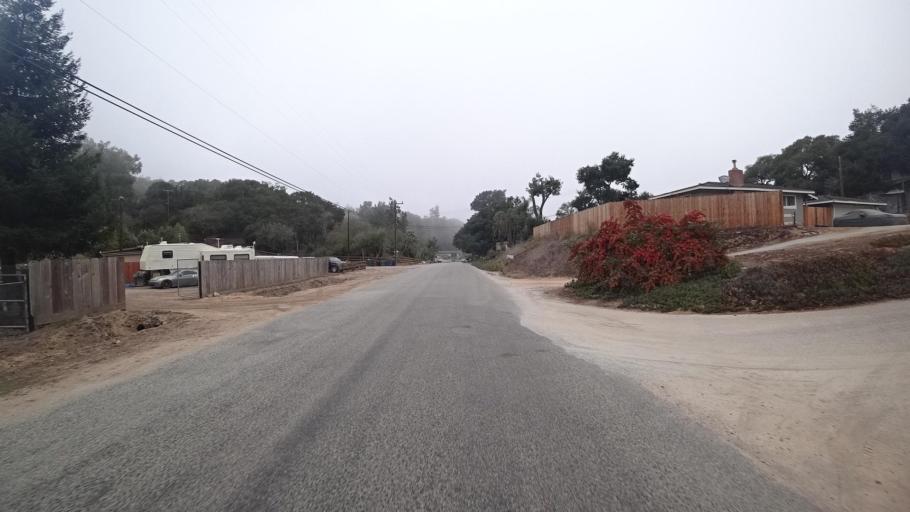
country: US
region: California
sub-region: Monterey County
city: Prunedale
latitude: 36.8109
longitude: -121.6341
